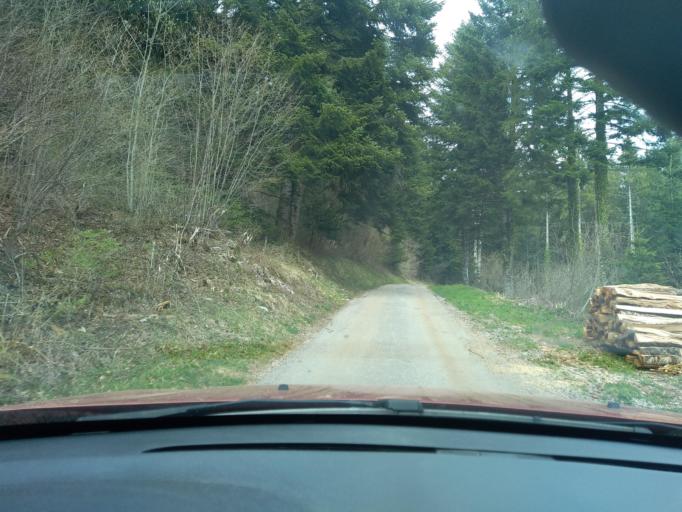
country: FR
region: Franche-Comte
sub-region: Departement du Jura
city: Moirans-en-Montagne
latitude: 46.4660
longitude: 5.7489
